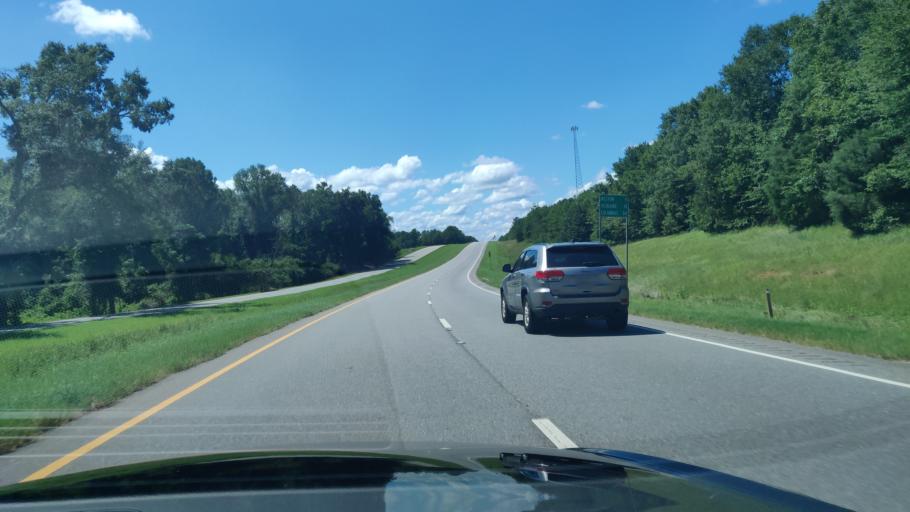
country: US
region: Georgia
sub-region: Terrell County
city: Dawson
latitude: 31.8731
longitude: -84.4944
